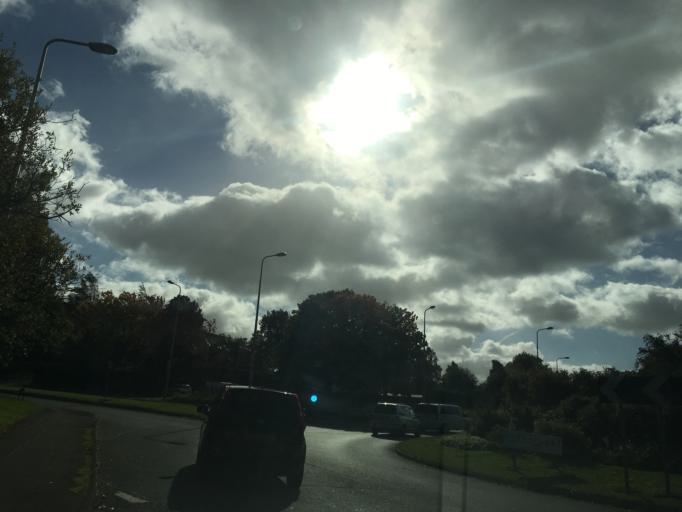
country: GB
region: Scotland
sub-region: Edinburgh
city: Currie
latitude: 55.9500
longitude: -3.3132
